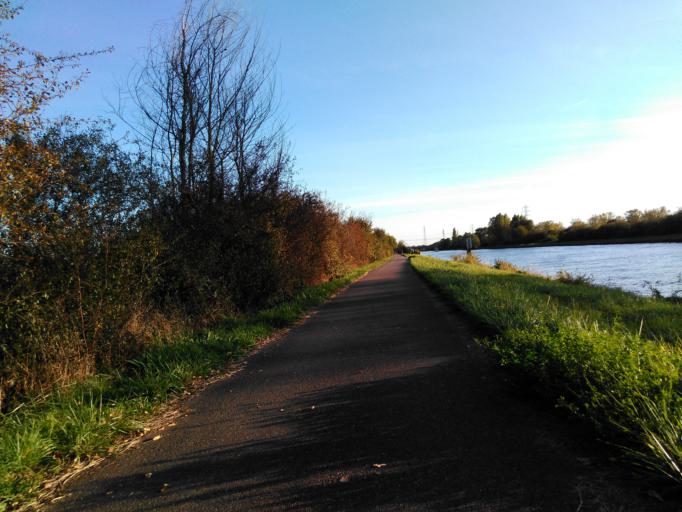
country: FR
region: Lorraine
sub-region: Departement de la Moselle
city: Maizieres-les-Metz
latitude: 49.2111
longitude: 6.1818
